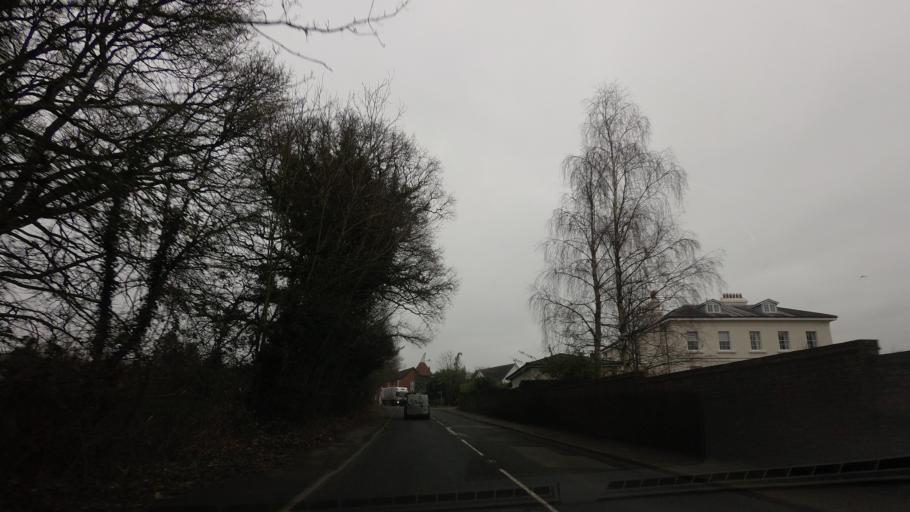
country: GB
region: England
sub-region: Kent
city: Hawkhurst
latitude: 51.0607
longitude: 0.5062
